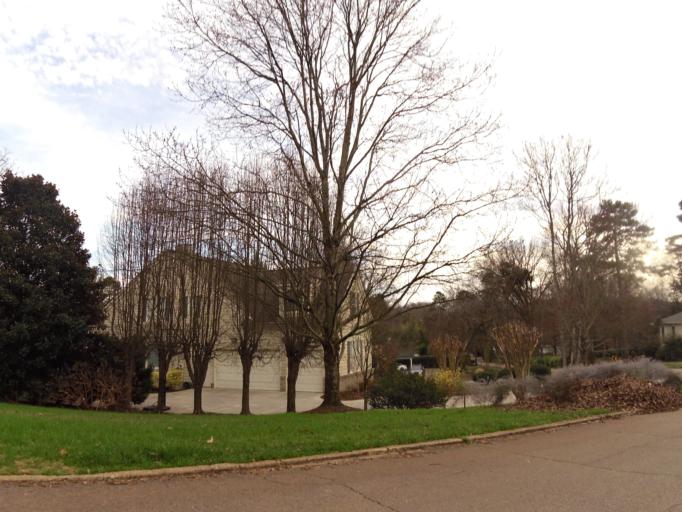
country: US
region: Tennessee
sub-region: Knox County
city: Knoxville
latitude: 35.9348
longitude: -83.9698
